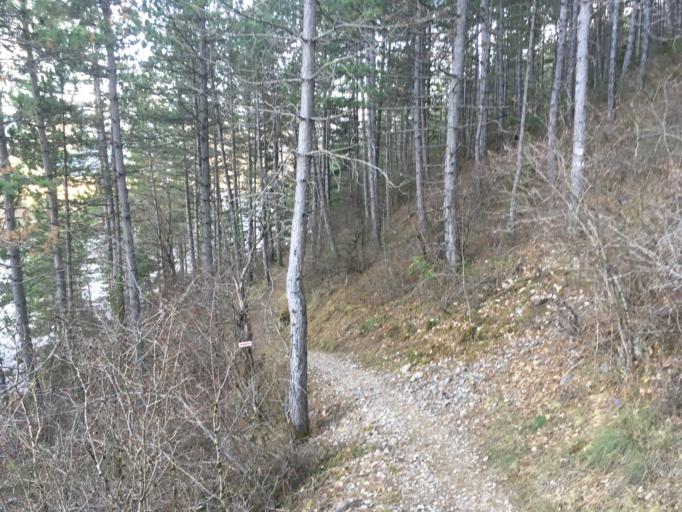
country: FR
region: Provence-Alpes-Cote d'Azur
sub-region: Departement des Alpes-de-Haute-Provence
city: Digne-les-Bains
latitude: 44.1073
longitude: 6.2270
